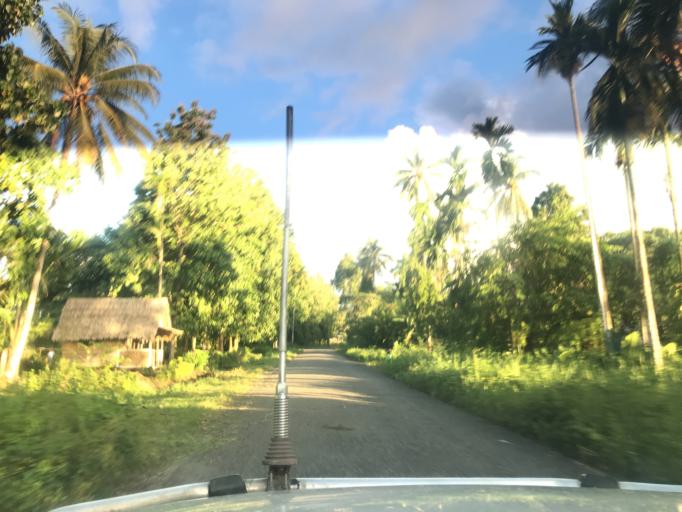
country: SB
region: Malaita
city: Auki
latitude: -8.7186
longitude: 160.7037
